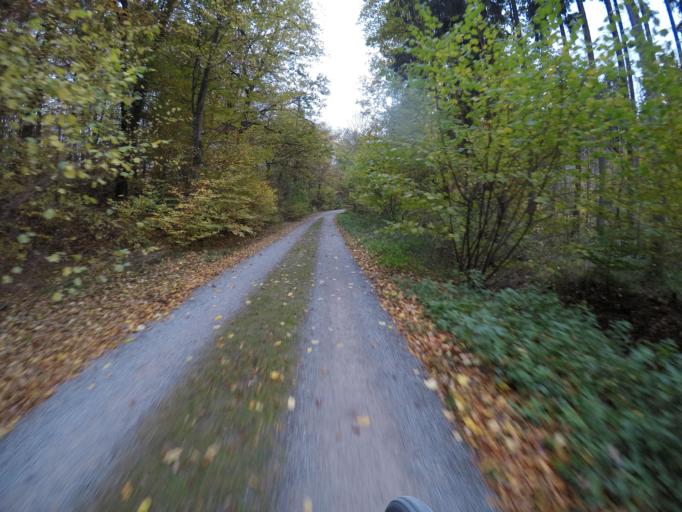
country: DE
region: Baden-Wuerttemberg
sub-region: Regierungsbezirk Stuttgart
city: Ehningen
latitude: 48.6653
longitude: 8.9586
